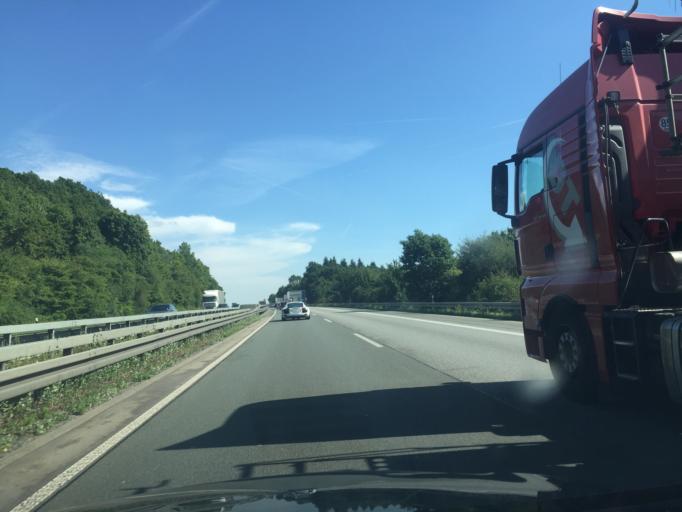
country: DE
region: Hesse
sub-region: Regierungsbezirk Giessen
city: Sinn
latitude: 50.6322
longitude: 8.3305
